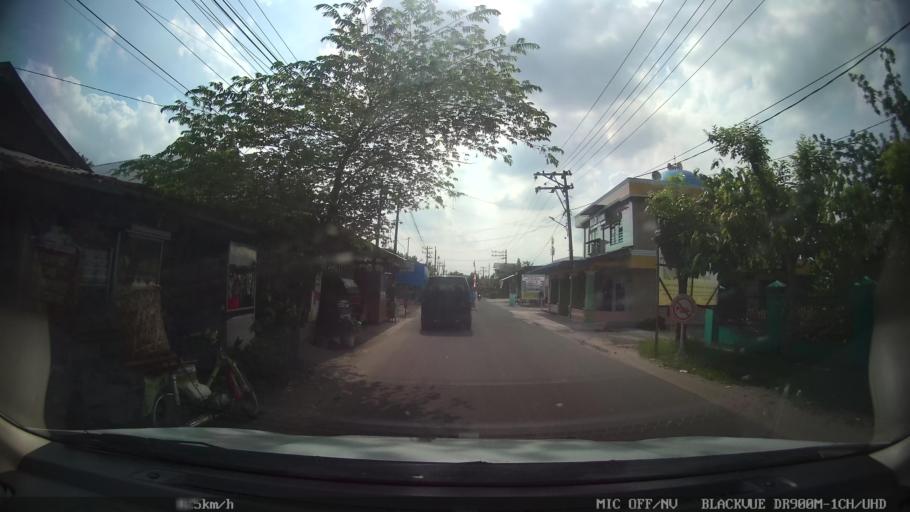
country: ID
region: North Sumatra
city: Binjai
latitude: 3.6439
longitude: 98.5020
